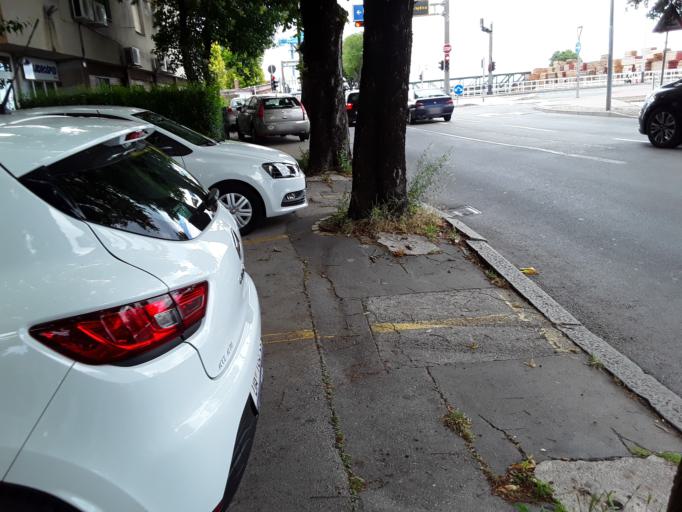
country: HR
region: Primorsko-Goranska
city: Drenova
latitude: 45.3241
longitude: 14.4494
